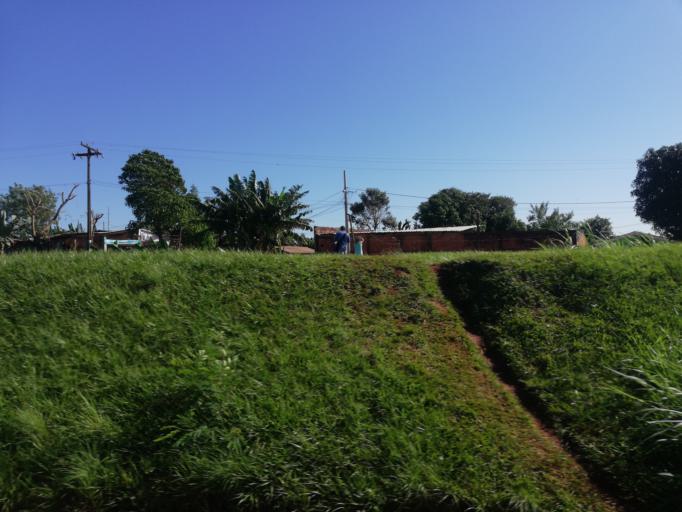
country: AR
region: Misiones
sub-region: Departamento de Iguazu
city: Puerto Iguazu
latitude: -25.5804
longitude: -54.5610
